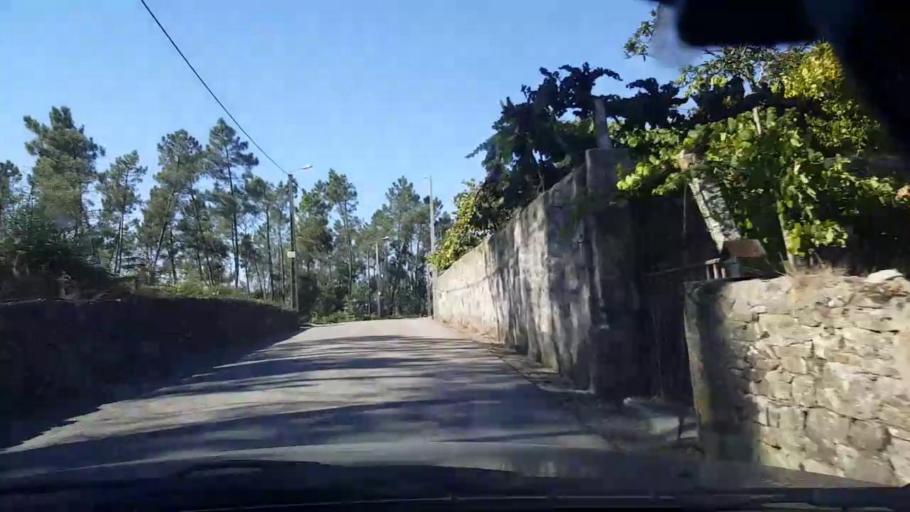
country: PT
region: Porto
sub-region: Vila do Conde
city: Arvore
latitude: 41.3653
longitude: -8.6463
